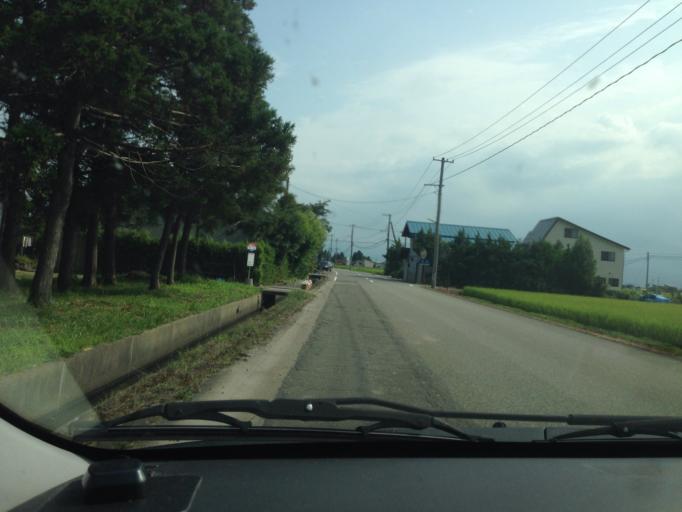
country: JP
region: Fukushima
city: Kitakata
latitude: 37.5719
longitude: 139.8535
